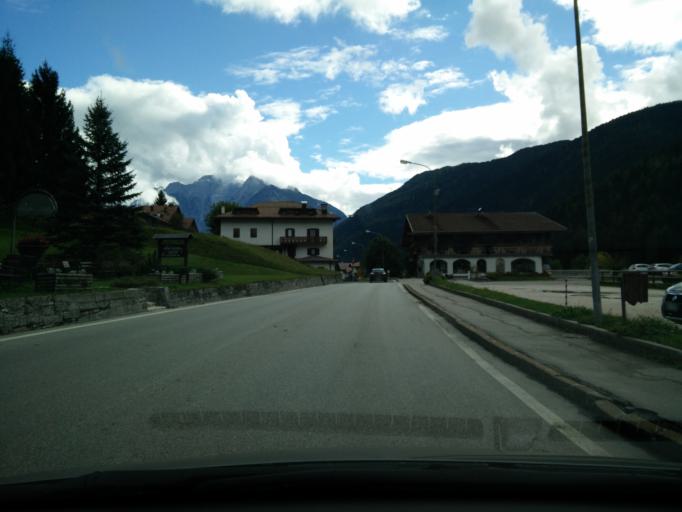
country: IT
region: Veneto
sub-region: Provincia di Belluno
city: Auronzo
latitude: 46.5600
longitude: 12.4210
